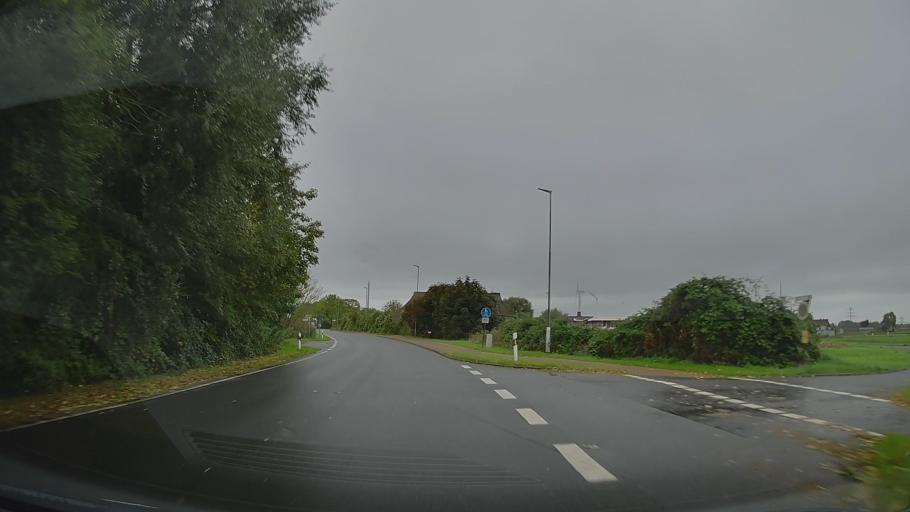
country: DE
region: Schleswig-Holstein
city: Buttel
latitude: 53.8982
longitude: 9.2339
